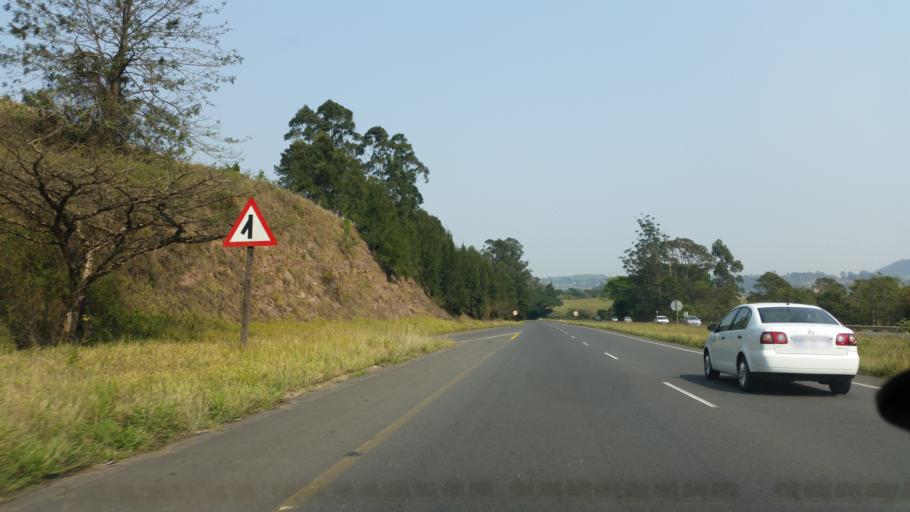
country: ZA
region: KwaZulu-Natal
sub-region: eThekwini Metropolitan Municipality
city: Mpumalanga
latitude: -29.7989
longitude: 30.7617
